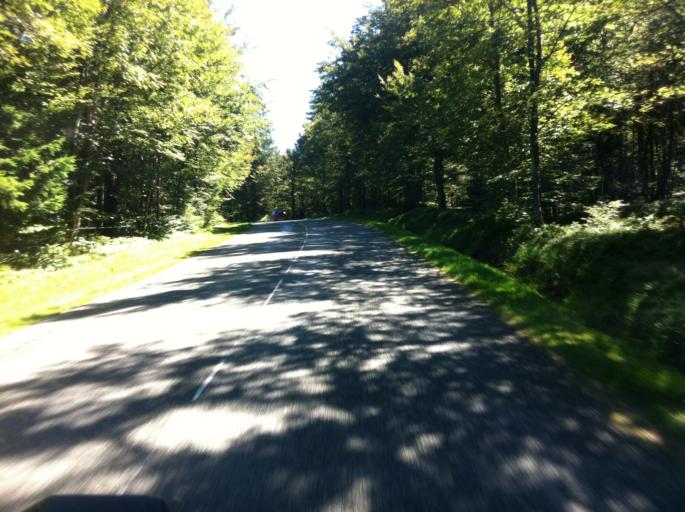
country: FR
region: Alsace
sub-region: Departement du Haut-Rhin
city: Soultzeren
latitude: 48.0909
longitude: 7.0544
